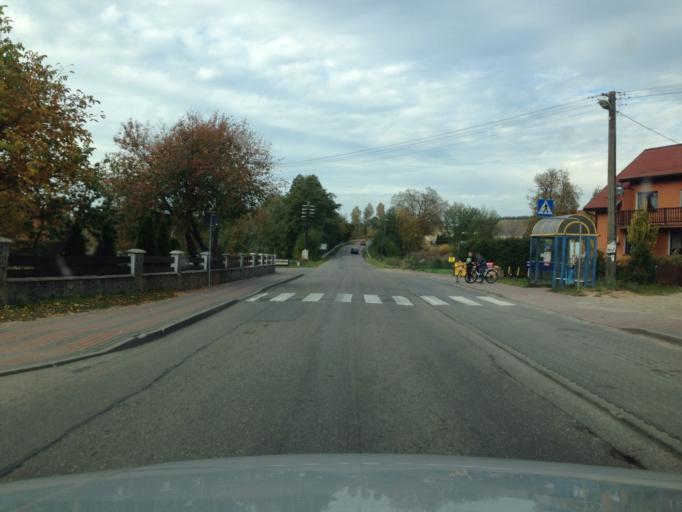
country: PL
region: Pomeranian Voivodeship
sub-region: Powiat kartuski
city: Stezyca
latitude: 54.1680
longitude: 17.9678
